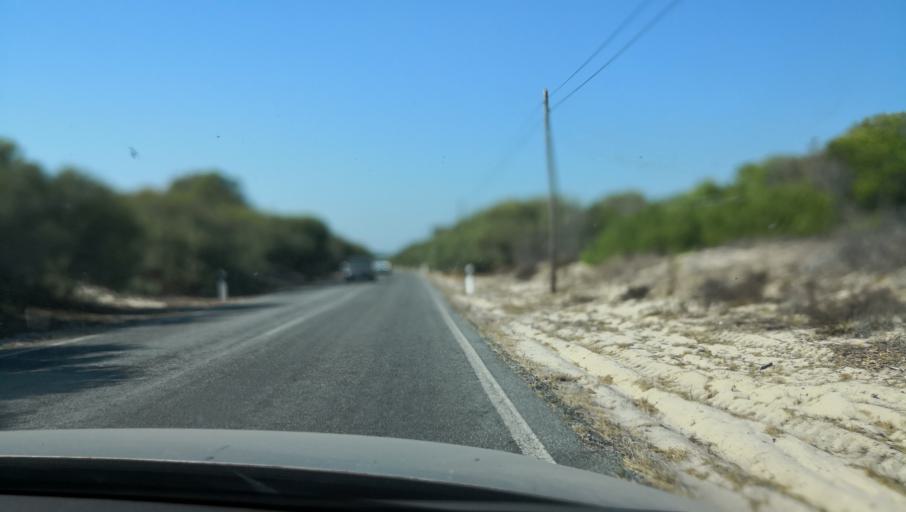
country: PT
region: Setubal
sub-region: Setubal
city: Setubal
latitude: 38.4075
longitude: -8.8107
